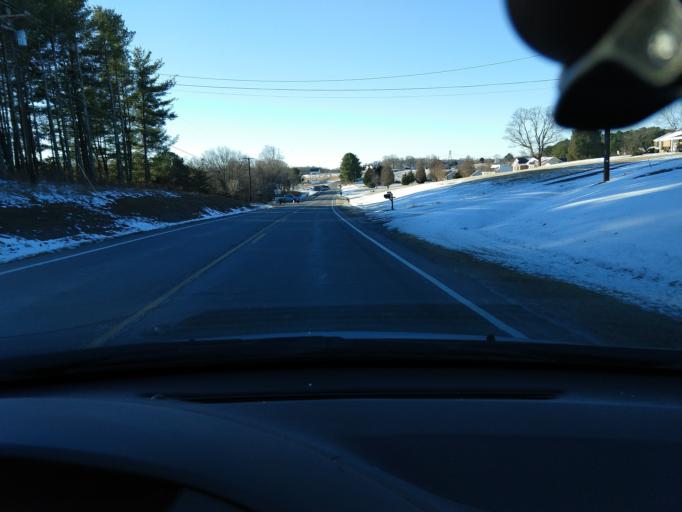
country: US
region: Virginia
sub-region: City of Bedford
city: Bedford
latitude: 37.3012
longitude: -79.5366
